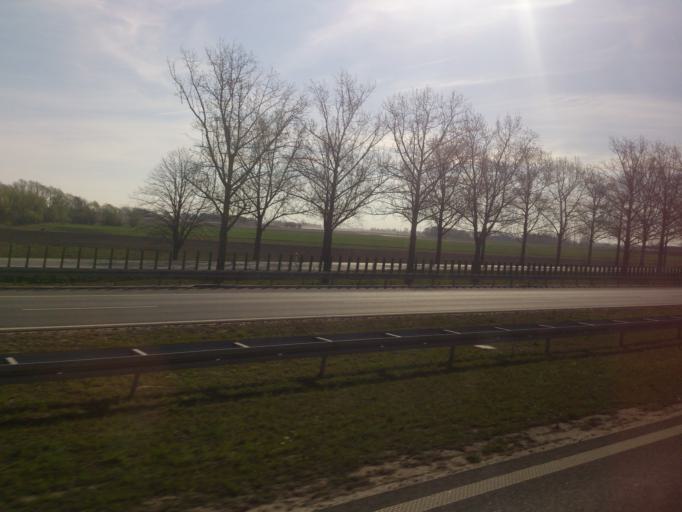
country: PL
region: Kujawsko-Pomorskie
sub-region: Powiat aleksandrowski
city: Raciazek
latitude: 52.8127
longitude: 18.8116
